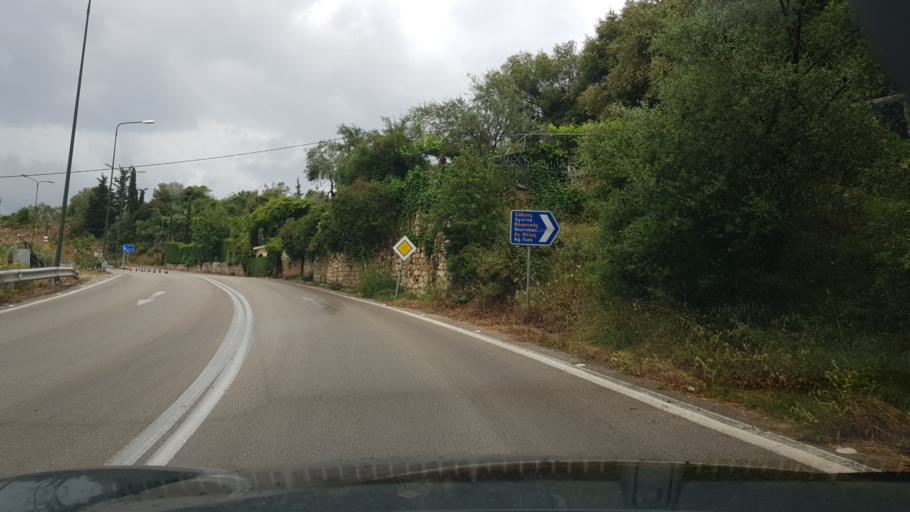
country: GR
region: Ionian Islands
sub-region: Lefkada
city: Nidri
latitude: 38.6518
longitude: 20.6822
